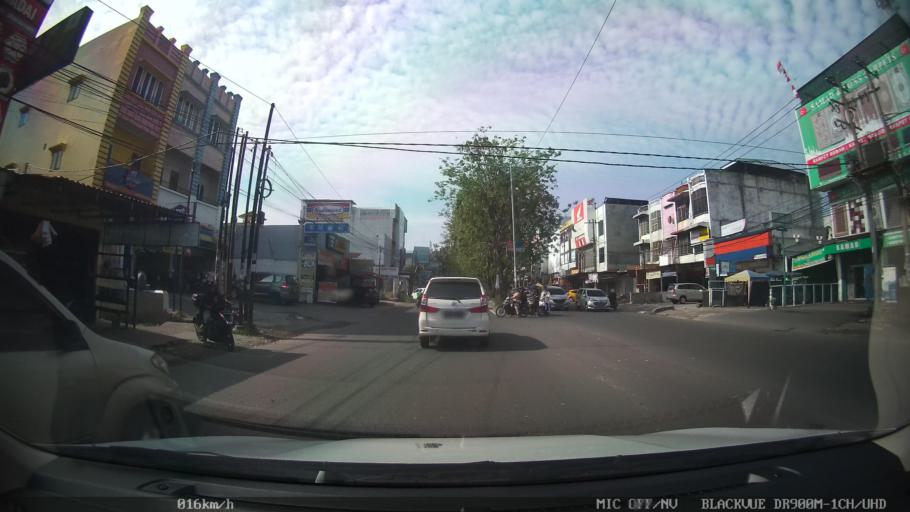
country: ID
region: North Sumatra
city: Medan
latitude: 3.5744
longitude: 98.6428
